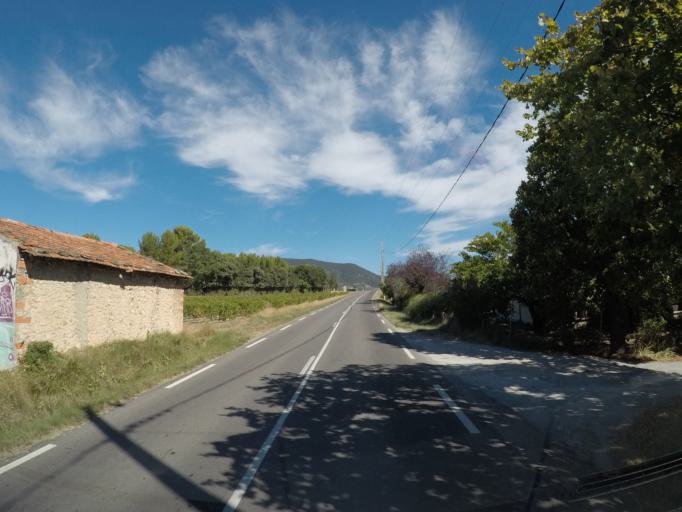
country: FR
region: Rhone-Alpes
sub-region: Departement de la Drome
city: Mirabel-aux-Baronnies
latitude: 44.3430
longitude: 5.1035
